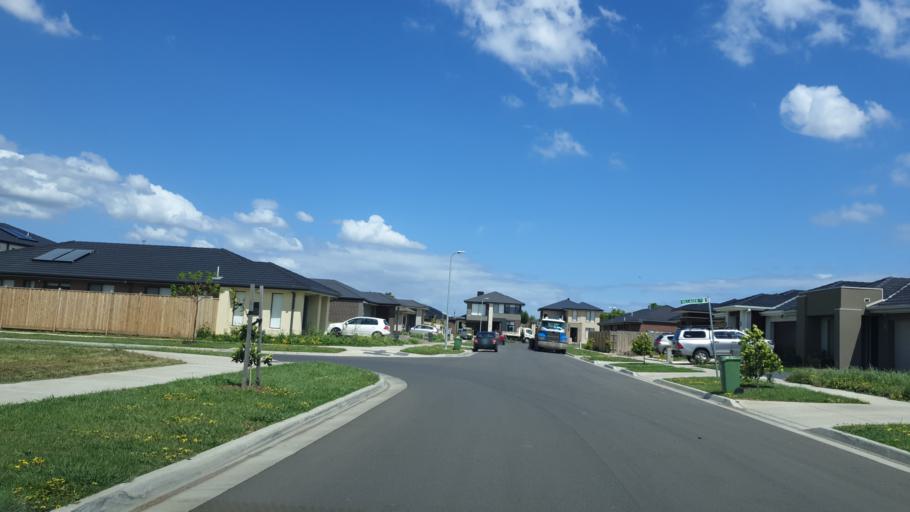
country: AU
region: Victoria
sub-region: Casey
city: Cranbourne
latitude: -38.0940
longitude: 145.2967
